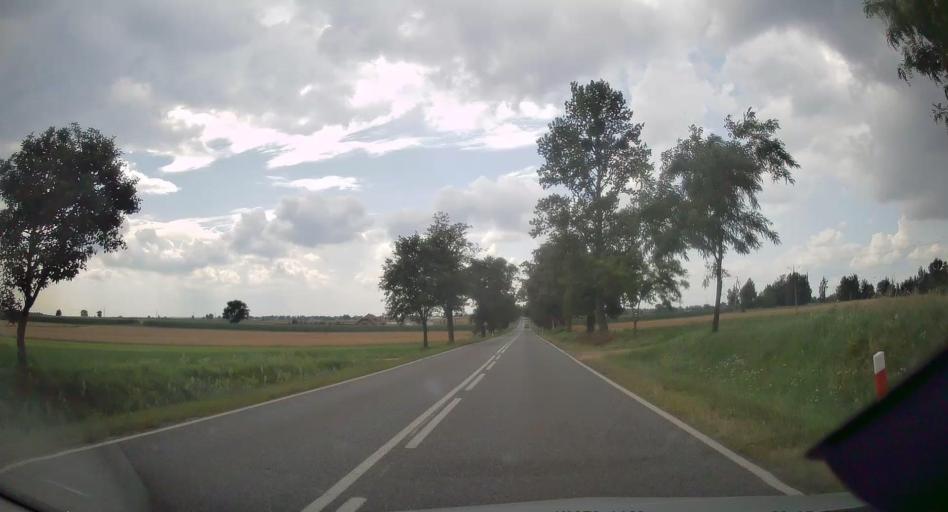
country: PL
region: Lodz Voivodeship
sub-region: Powiat skierniewicki
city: Gluchow
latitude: 51.7777
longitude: 20.1043
